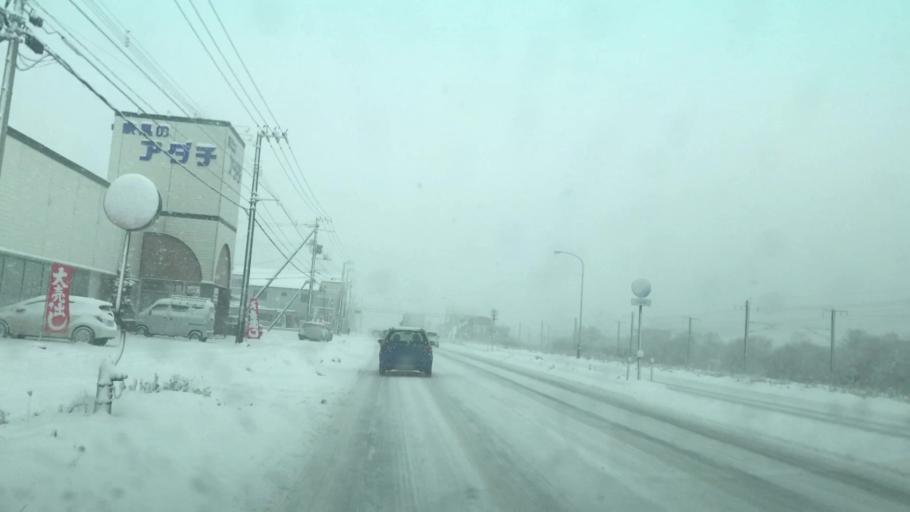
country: JP
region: Hokkaido
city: Muroran
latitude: 42.3864
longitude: 141.0790
